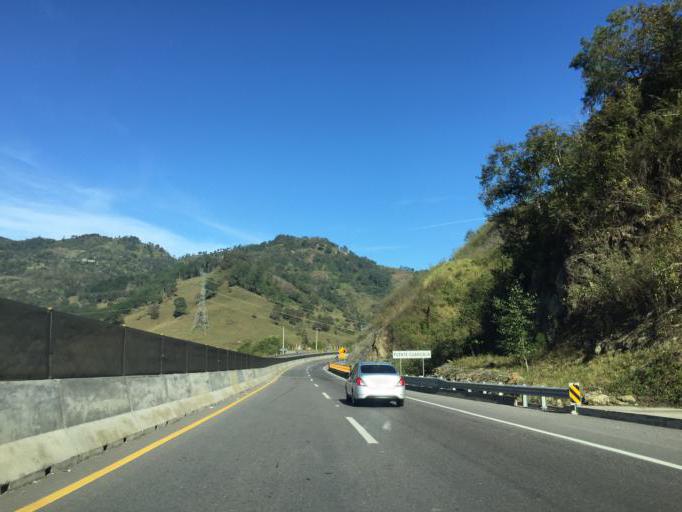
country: MX
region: Puebla
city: Necaxa
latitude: 20.2393
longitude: -98.0340
